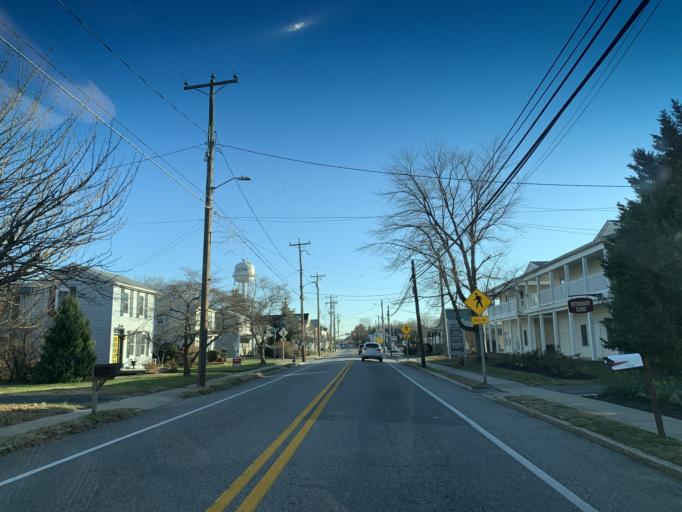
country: US
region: Delaware
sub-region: New Castle County
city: Townsend
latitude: 39.3427
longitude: -75.8793
